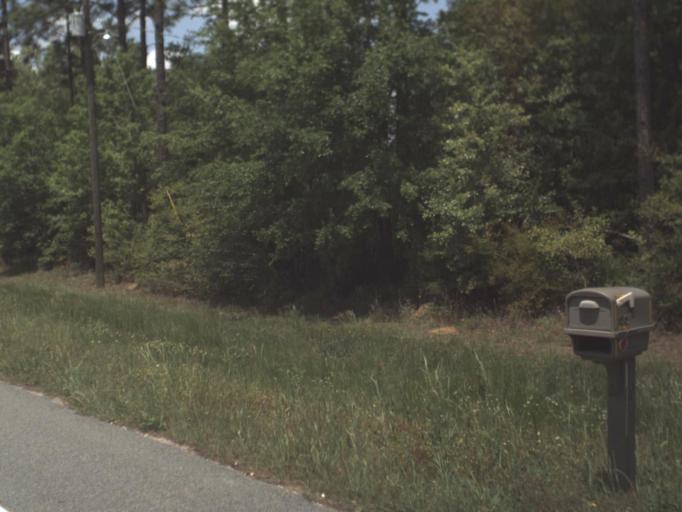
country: US
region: Florida
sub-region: Escambia County
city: Molino
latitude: 30.7961
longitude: -87.4211
